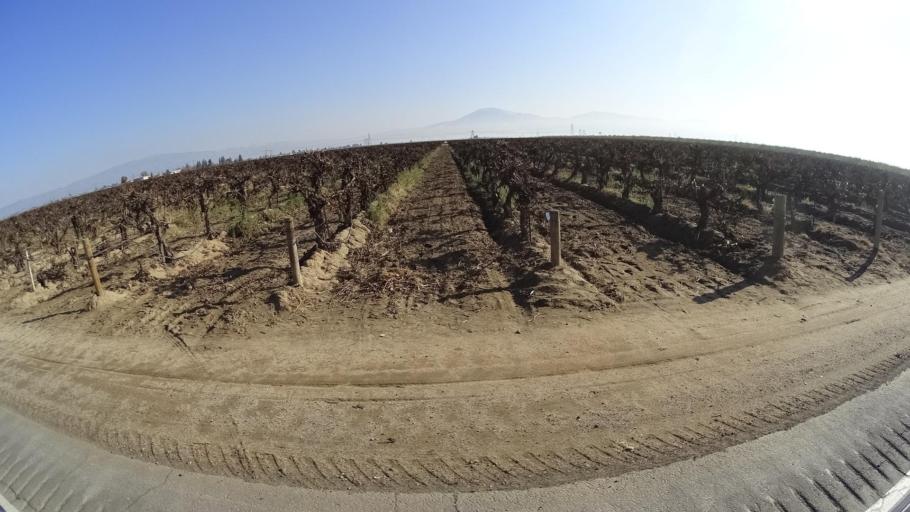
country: US
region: California
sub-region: Kern County
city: Weedpatch
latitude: 35.2319
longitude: -118.9322
